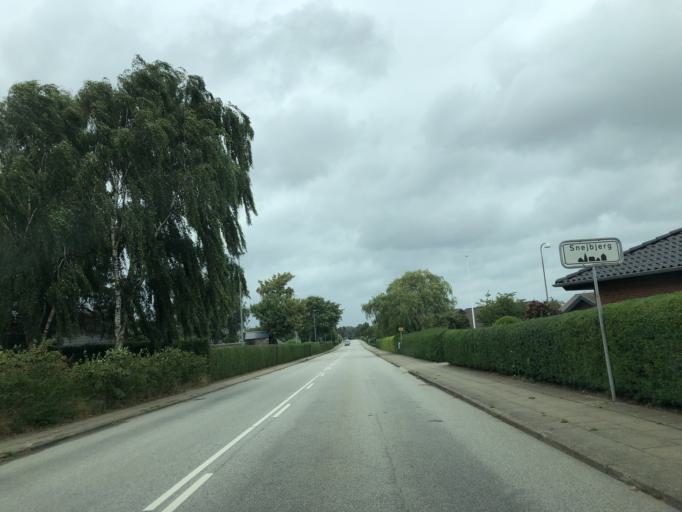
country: DK
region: Central Jutland
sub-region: Herning Kommune
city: Snejbjerg
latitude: 56.1259
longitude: 8.8960
